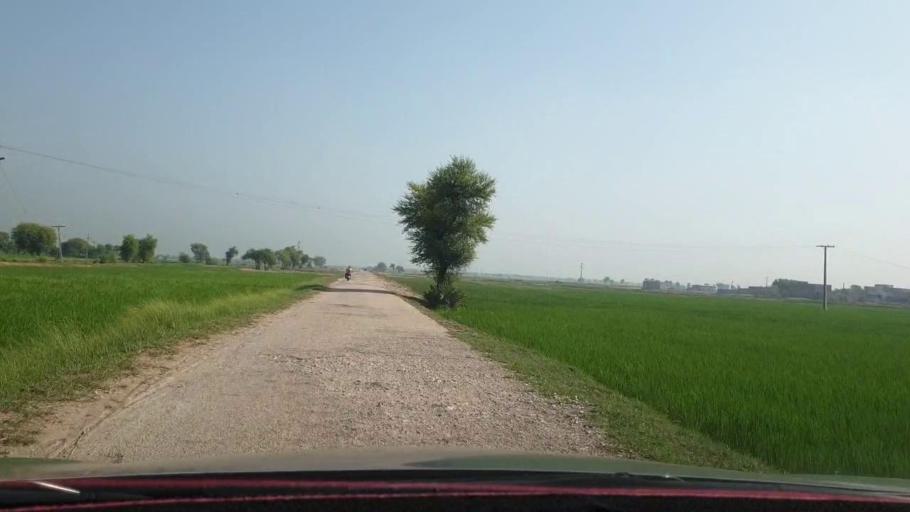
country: PK
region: Sindh
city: Nasirabad
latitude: 27.4929
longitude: 67.9286
